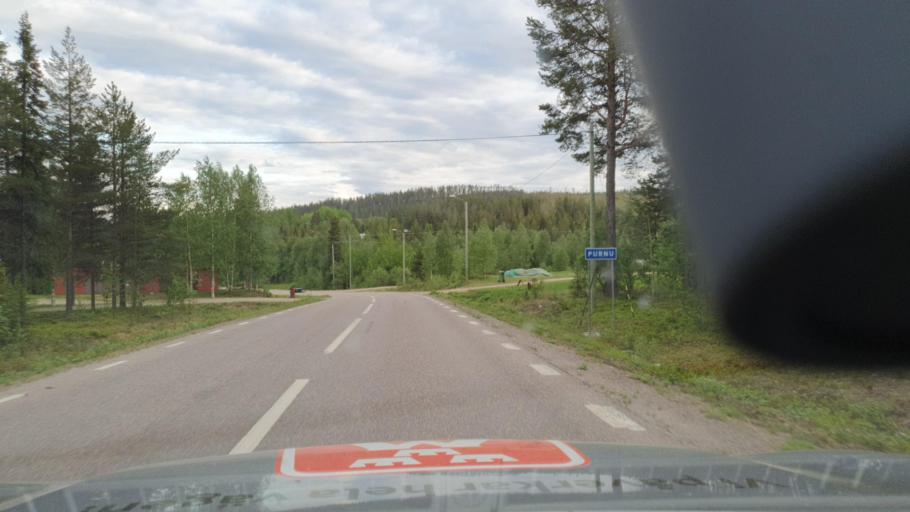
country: SE
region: Norrbotten
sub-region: Gallivare Kommun
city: Gaellivare
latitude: 66.8925
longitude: 21.2883
